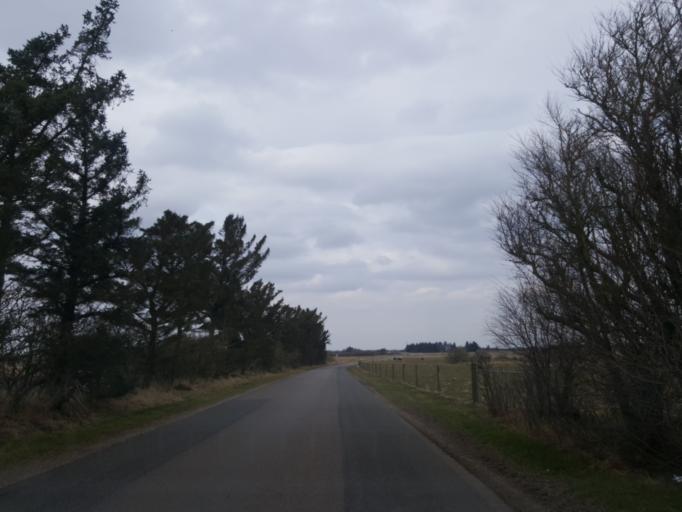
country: DK
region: Central Jutland
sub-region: Lemvig Kommune
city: Lemvig
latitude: 56.4056
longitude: 8.2332
